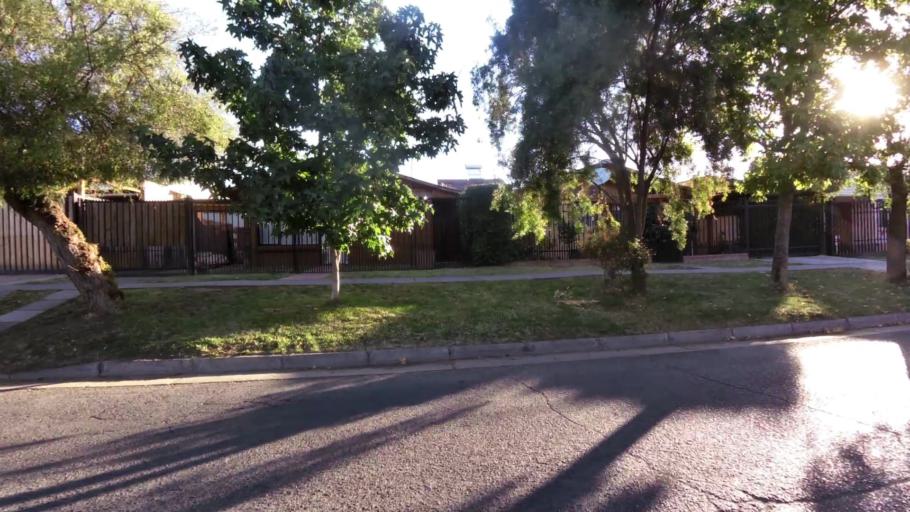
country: CL
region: O'Higgins
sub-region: Provincia de Cachapoal
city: Rancagua
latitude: -34.1741
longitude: -70.7627
